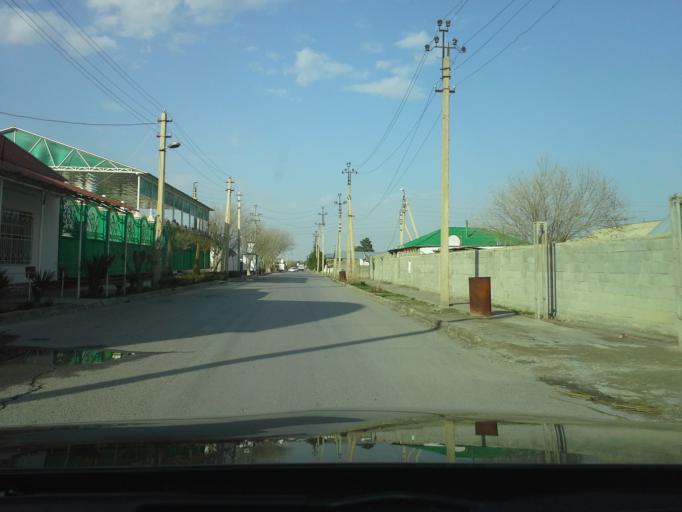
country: TM
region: Ahal
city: Abadan
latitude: 38.0201
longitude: 58.2349
